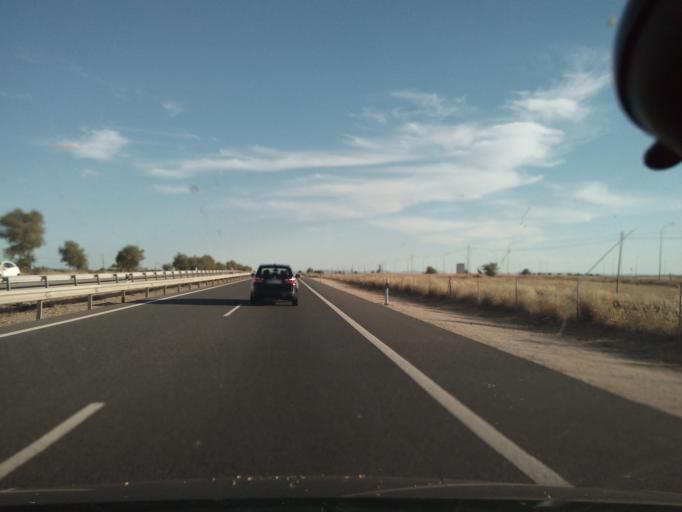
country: ES
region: Castille-La Mancha
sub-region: Province of Toledo
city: Tembleque
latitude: 39.7721
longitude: -3.4797
